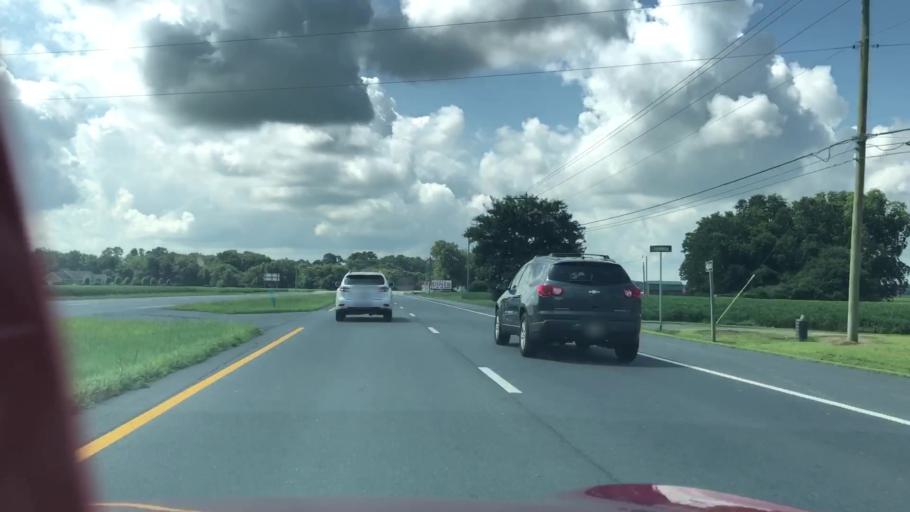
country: US
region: Virginia
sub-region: Accomack County
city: Accomac
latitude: 37.7747
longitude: -75.6119
